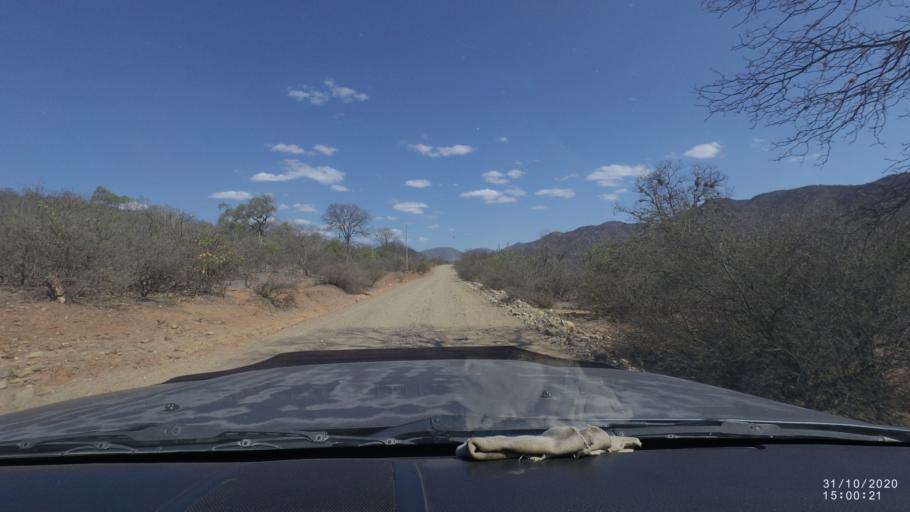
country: BO
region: Cochabamba
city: Aiquile
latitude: -18.2567
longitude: -64.8254
